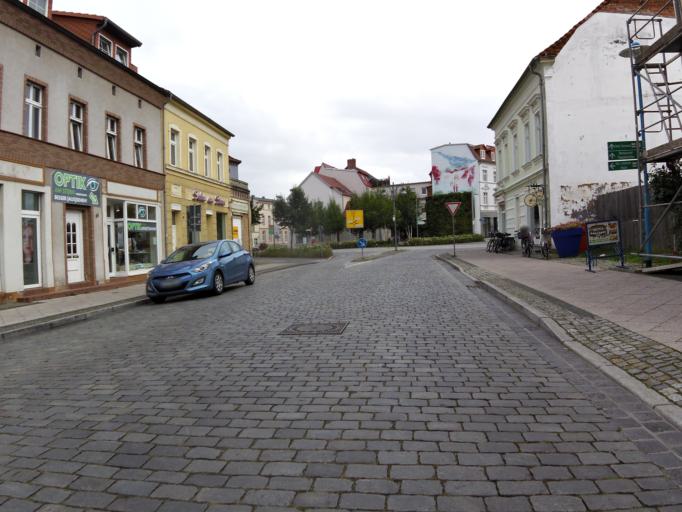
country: DE
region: Brandenburg
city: Wittenberge
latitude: 52.9943
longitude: 11.7528
